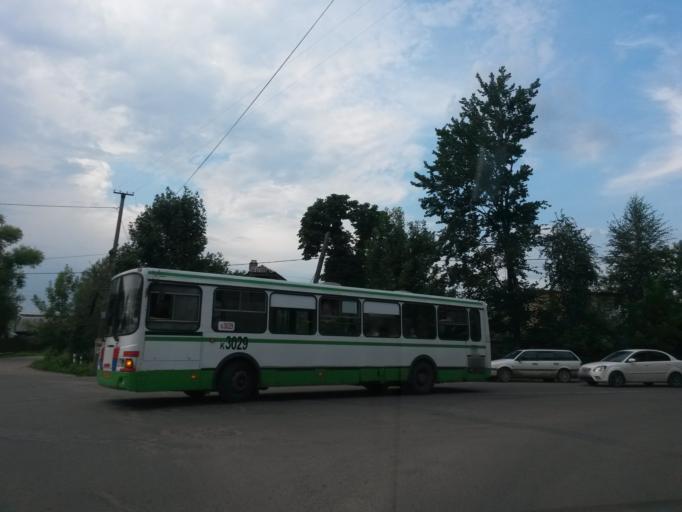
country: RU
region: Jaroslavl
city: Yaroslavl
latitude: 57.6076
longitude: 39.8133
